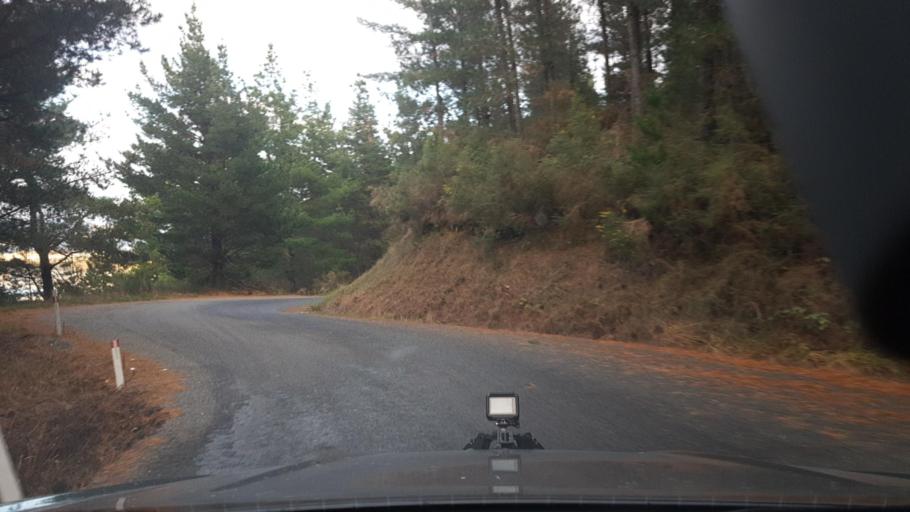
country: NZ
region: Nelson
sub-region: Nelson City
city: Nelson
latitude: -41.5820
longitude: 173.4179
